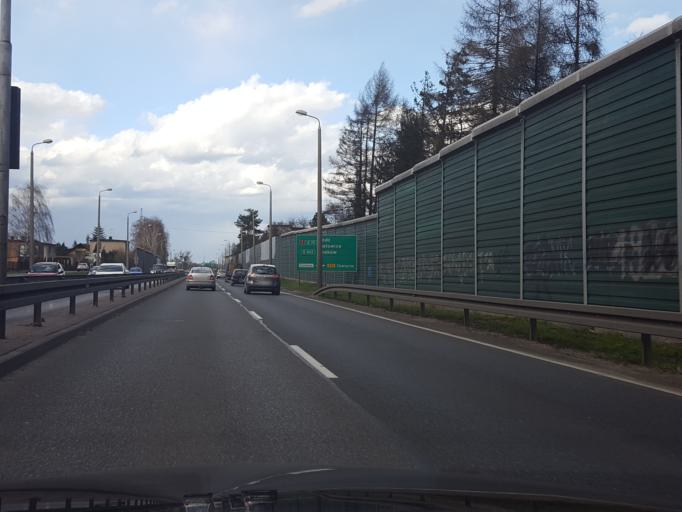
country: PL
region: Silesian Voivodeship
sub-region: Powiat pszczynski
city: Pszczyna
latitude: 49.9703
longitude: 18.9583
